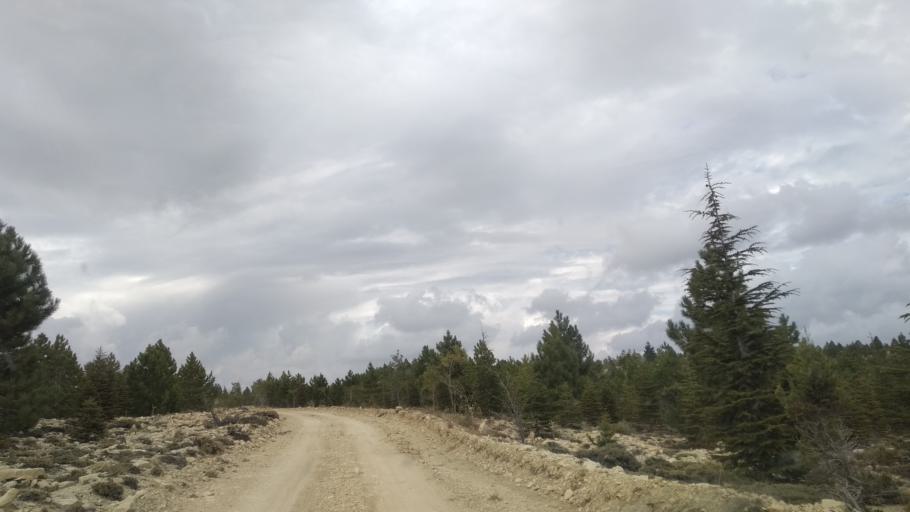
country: TR
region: Mersin
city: Sarikavak
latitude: 36.5716
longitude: 33.7553
